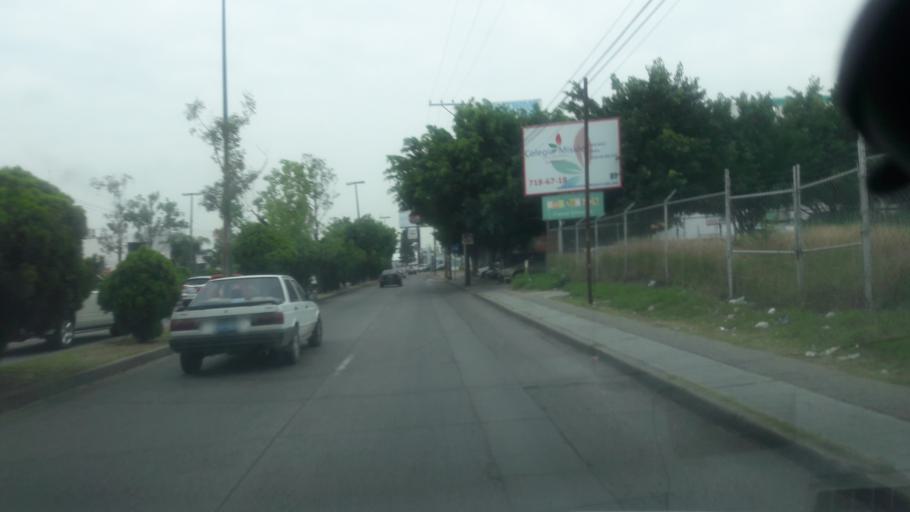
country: MX
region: Guanajuato
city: Leon
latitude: 21.1454
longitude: -101.6992
